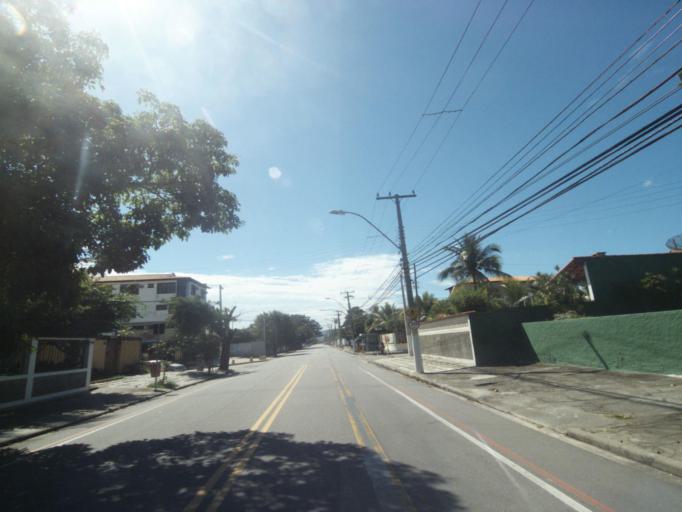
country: BR
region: Rio de Janeiro
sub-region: Niteroi
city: Niteroi
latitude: -22.9518
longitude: -43.0895
